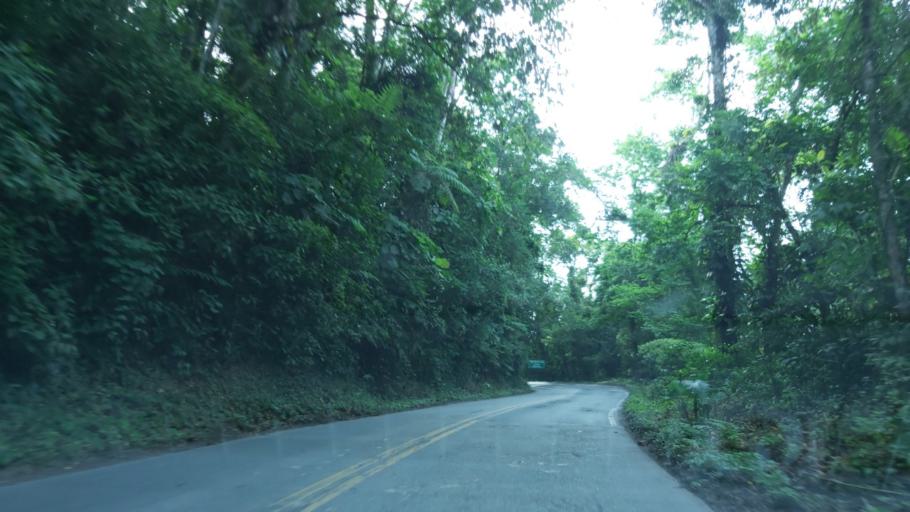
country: BR
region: Sao Paulo
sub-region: Juquia
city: Juquia
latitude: -24.0980
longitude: -47.6197
